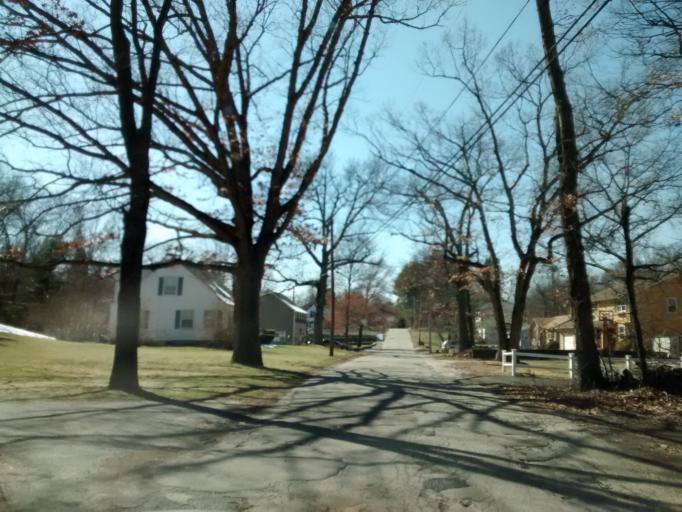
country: US
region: Massachusetts
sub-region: Worcester County
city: Millbury
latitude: 42.1872
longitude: -71.7499
